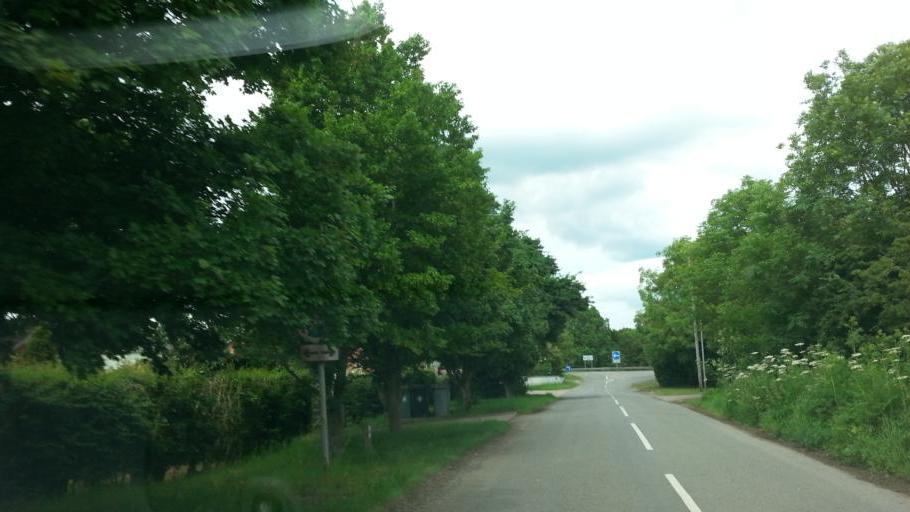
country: GB
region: England
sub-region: Lincolnshire
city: Long Bennington
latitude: 52.9708
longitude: -0.7222
